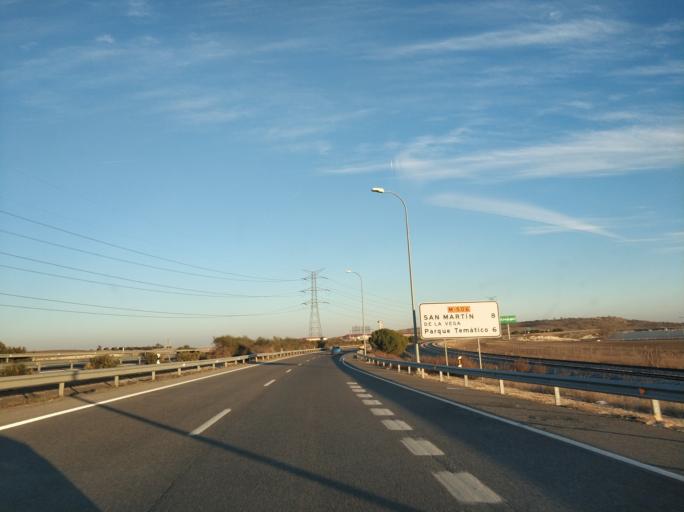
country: ES
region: Madrid
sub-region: Provincia de Madrid
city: Valdemoro
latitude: 40.2209
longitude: -3.6730
